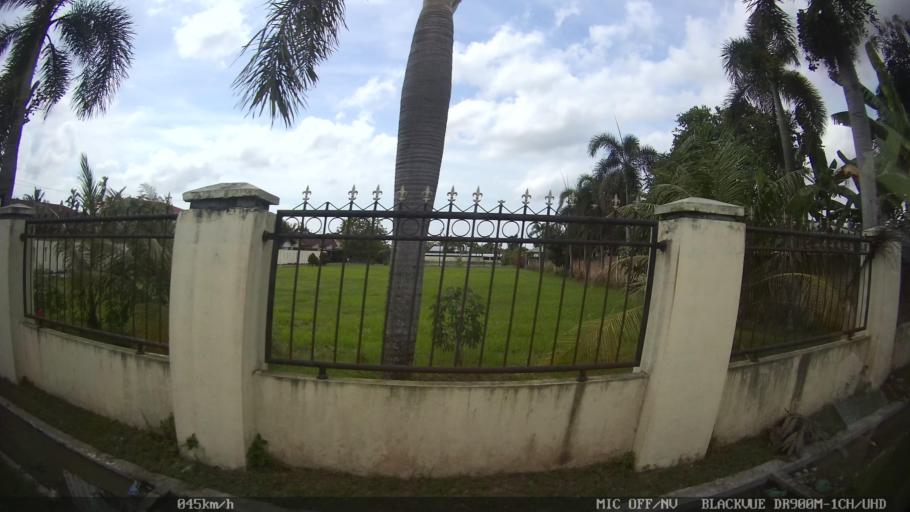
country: ID
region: North Sumatra
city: Percut
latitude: 3.5684
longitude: 98.8621
